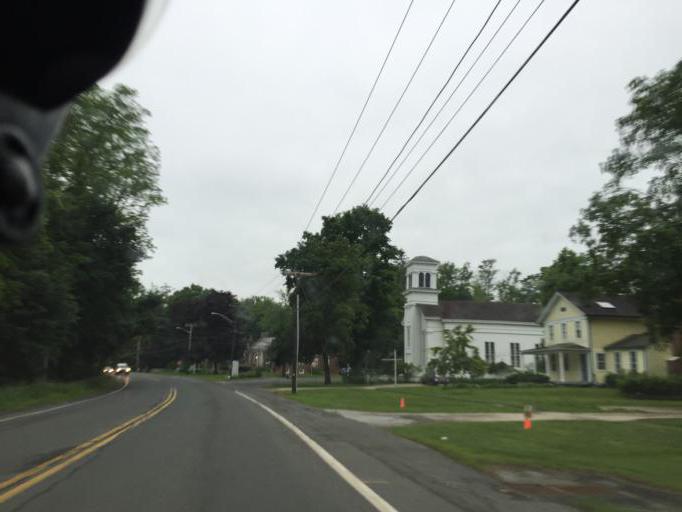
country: US
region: Massachusetts
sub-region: Berkshire County
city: Sheffield
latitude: 42.1080
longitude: -73.3549
